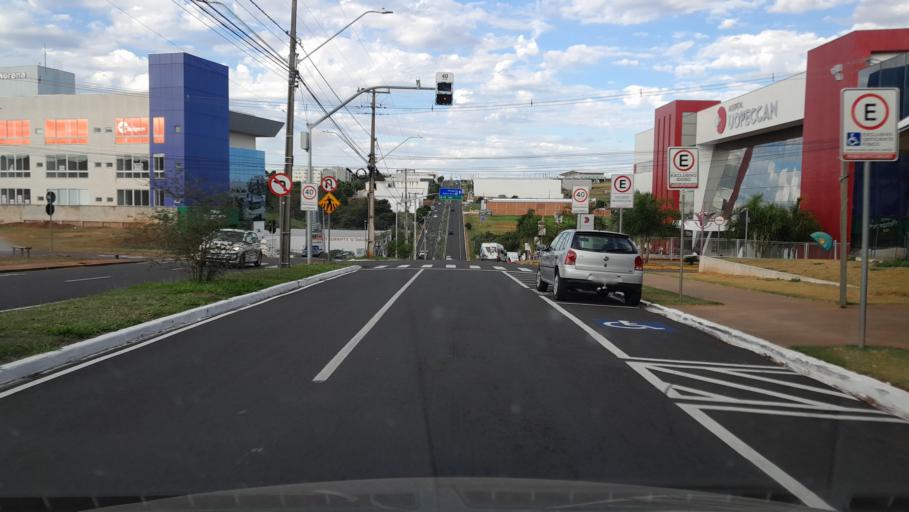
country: BR
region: Parana
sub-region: Umuarama
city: Umuarama
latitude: -23.7545
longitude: -53.2808
